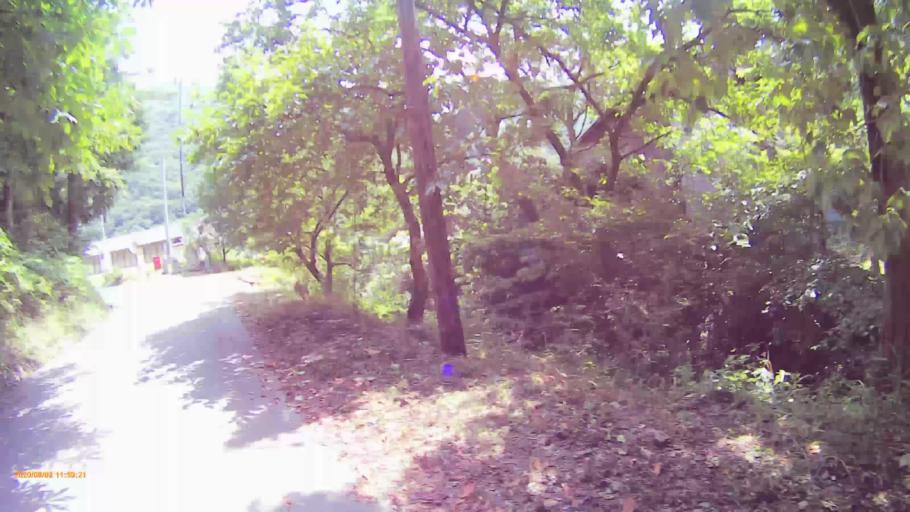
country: JP
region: Nagano
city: Shiojiri
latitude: 36.0236
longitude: 137.8684
